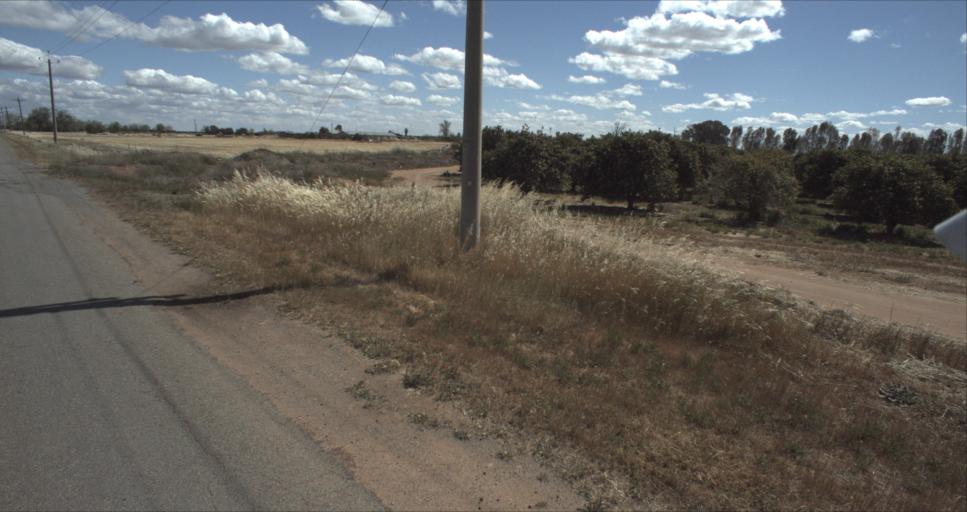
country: AU
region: New South Wales
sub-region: Leeton
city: Leeton
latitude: -34.5115
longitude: 146.2529
